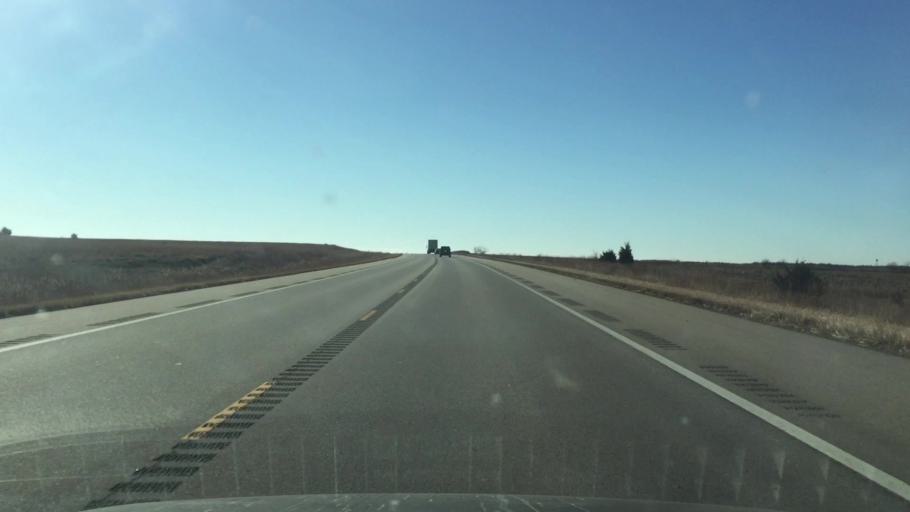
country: US
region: Kansas
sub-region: Allen County
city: Iola
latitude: 38.0633
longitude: -95.3802
